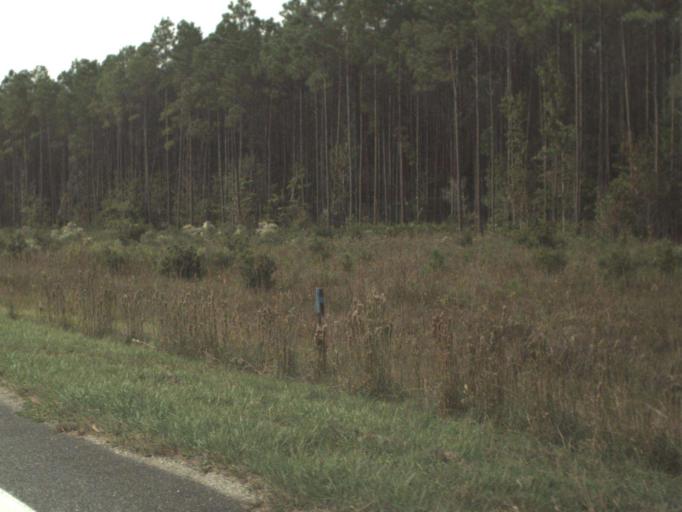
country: US
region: Florida
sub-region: Leon County
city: Woodville
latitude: 30.1950
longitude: -84.1374
